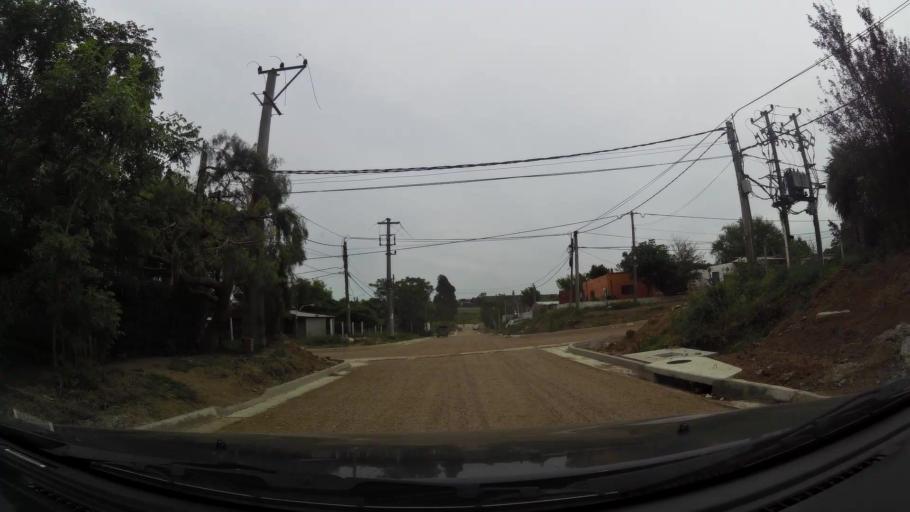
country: UY
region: Canelones
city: Las Piedras
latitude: -34.7435
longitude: -56.2175
